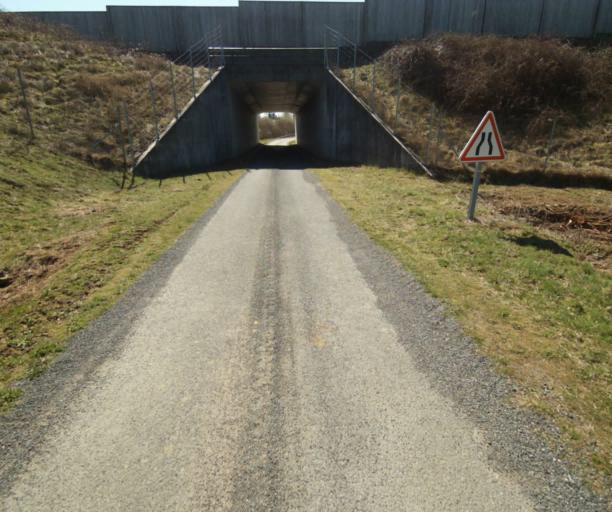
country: FR
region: Limousin
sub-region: Departement de la Correze
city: Saint-Clement
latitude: 45.3096
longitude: 1.6990
